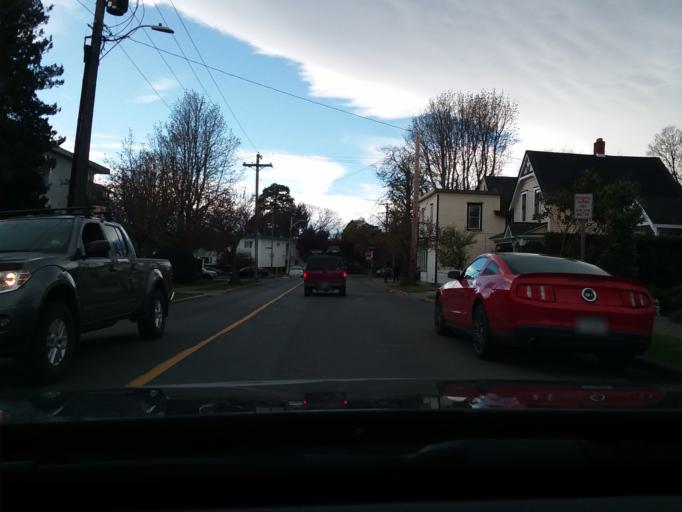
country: CA
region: British Columbia
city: Victoria
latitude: 48.4183
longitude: -123.3574
